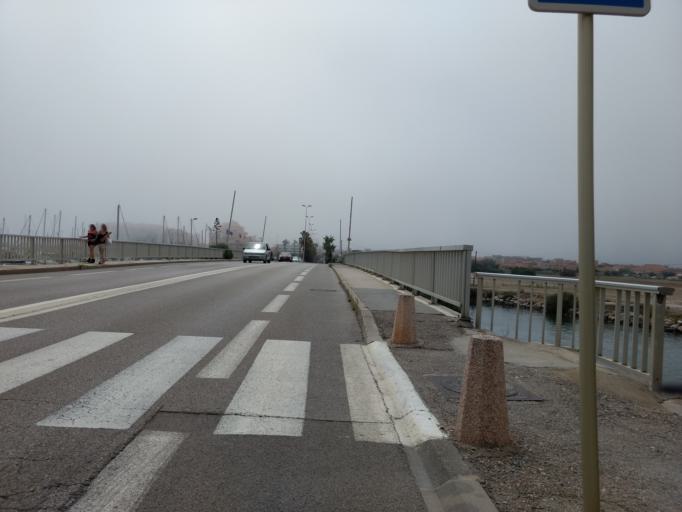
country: FR
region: Languedoc-Roussillon
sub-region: Departement des Pyrenees-Orientales
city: Le Barcares
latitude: 42.7985
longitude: 3.0367
